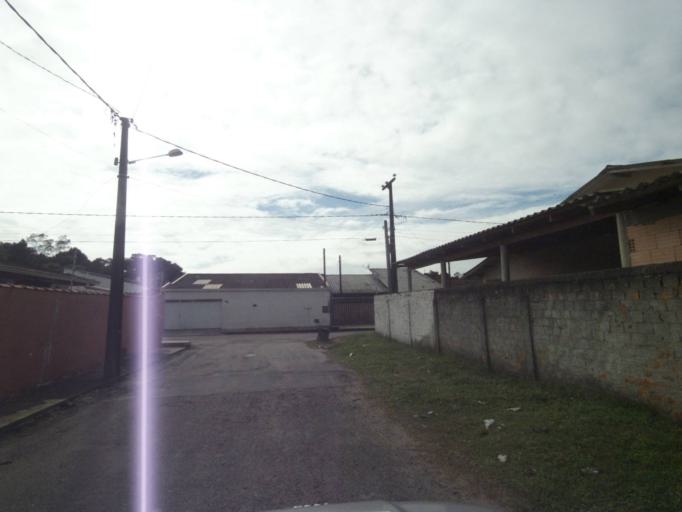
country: BR
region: Parana
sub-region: Paranagua
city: Paranagua
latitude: -25.5654
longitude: -48.5604
